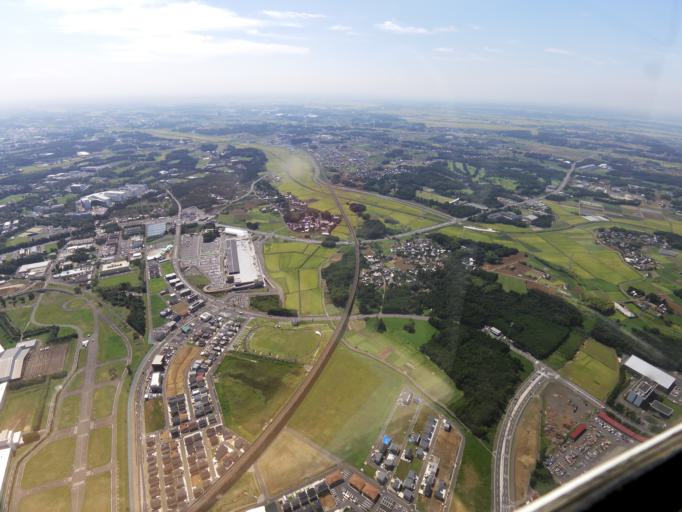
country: JP
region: Ibaraki
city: Naka
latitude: 36.0840
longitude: 140.0733
